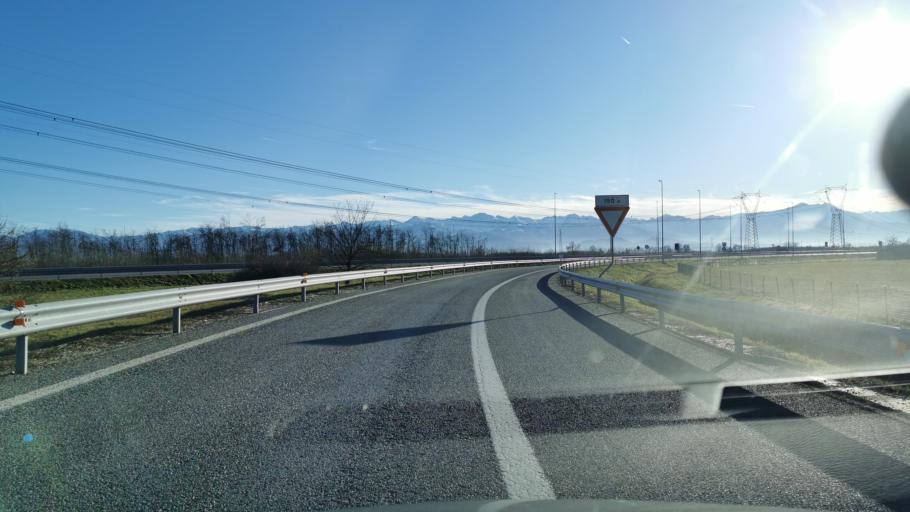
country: IT
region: Piedmont
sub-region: Provincia di Cuneo
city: Magliano Alpi
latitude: 44.4877
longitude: 7.8162
